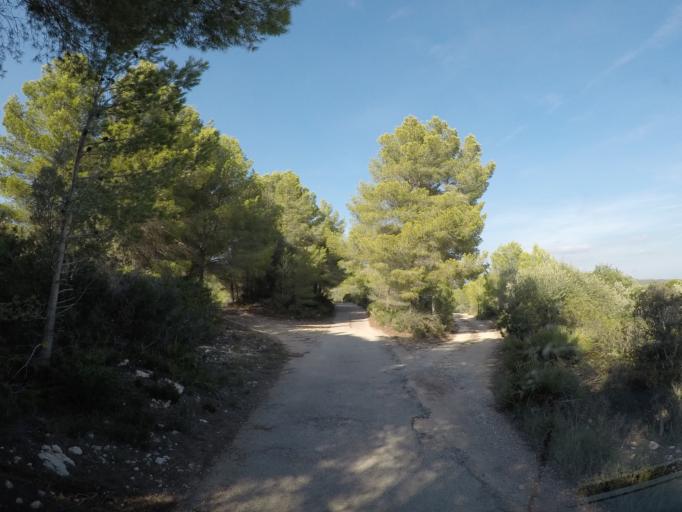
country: ES
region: Catalonia
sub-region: Provincia de Tarragona
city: El Perello
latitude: 40.9159
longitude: 0.7234
